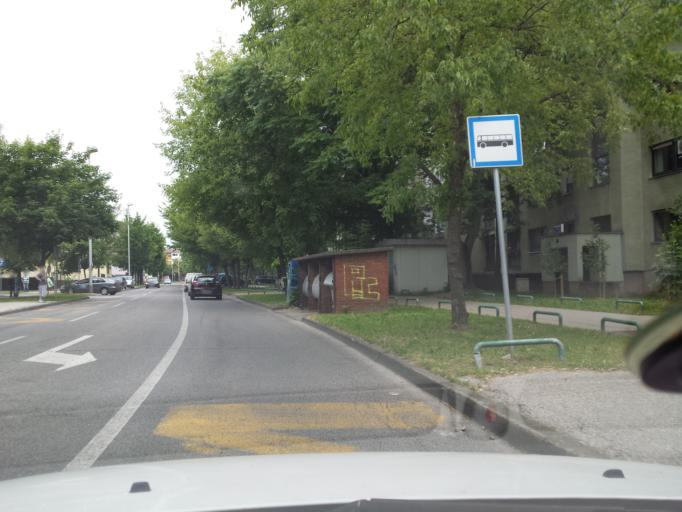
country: HR
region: Grad Zagreb
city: Jankomir
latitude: 45.7897
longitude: 15.9304
